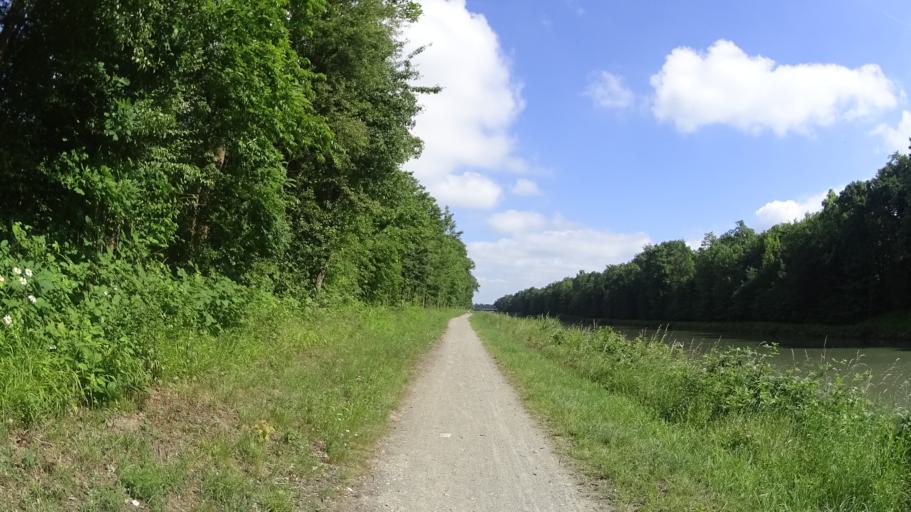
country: DE
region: Lower Saxony
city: Harsum
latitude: 52.2161
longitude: 9.9395
